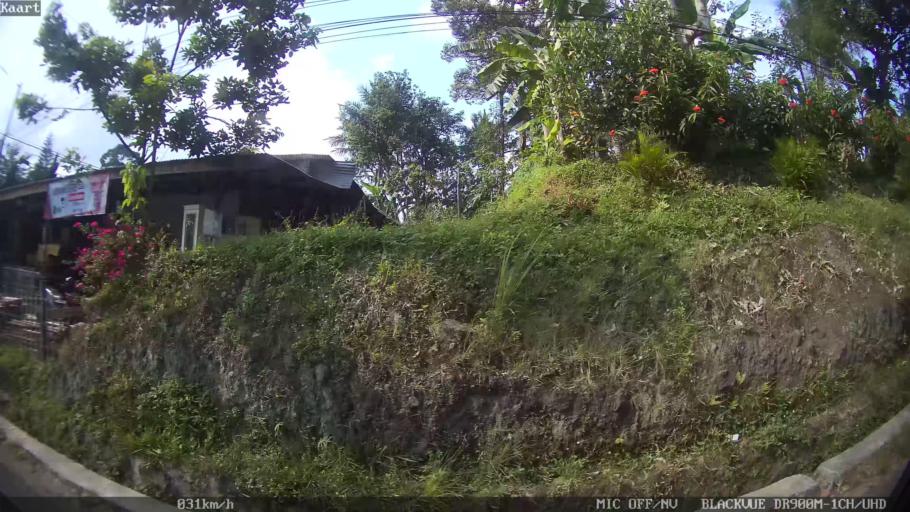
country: ID
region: Lampung
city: Kedaton
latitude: -5.3939
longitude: 105.2208
